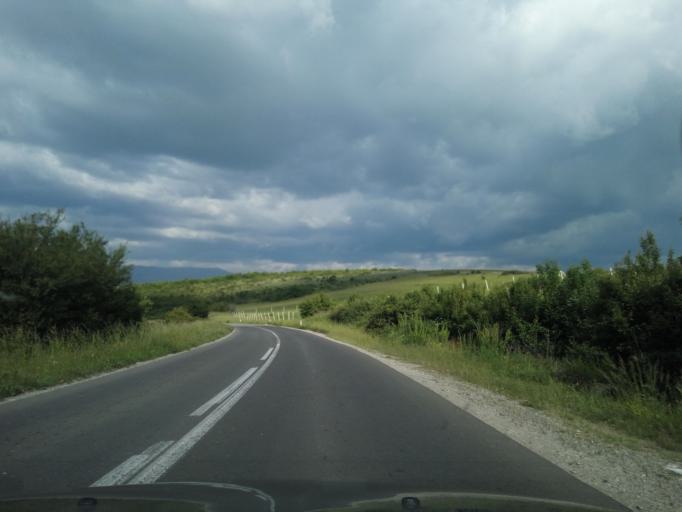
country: XK
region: Gjakova
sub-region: Komuna e Gjakoves
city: Gjakove
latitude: 42.4313
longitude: 20.4527
